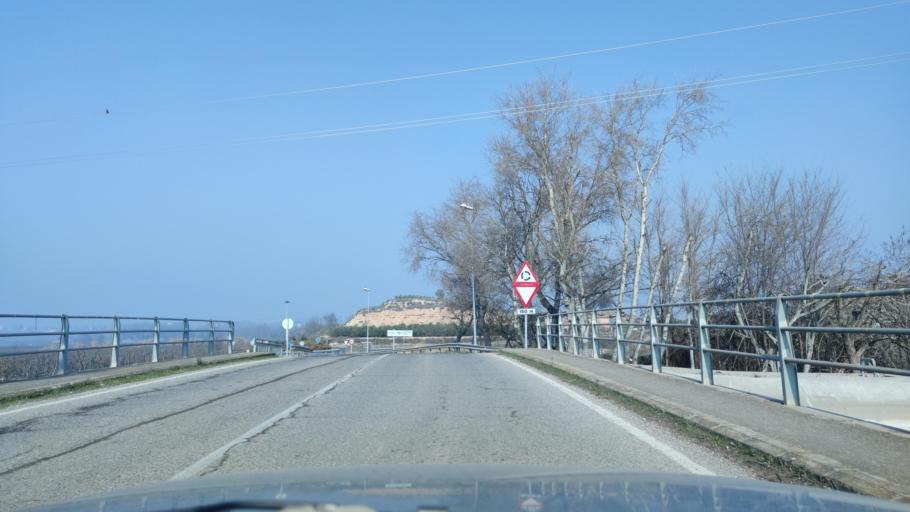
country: ES
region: Catalonia
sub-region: Provincia de Lleida
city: Sunyer
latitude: 41.5627
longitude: 0.5875
